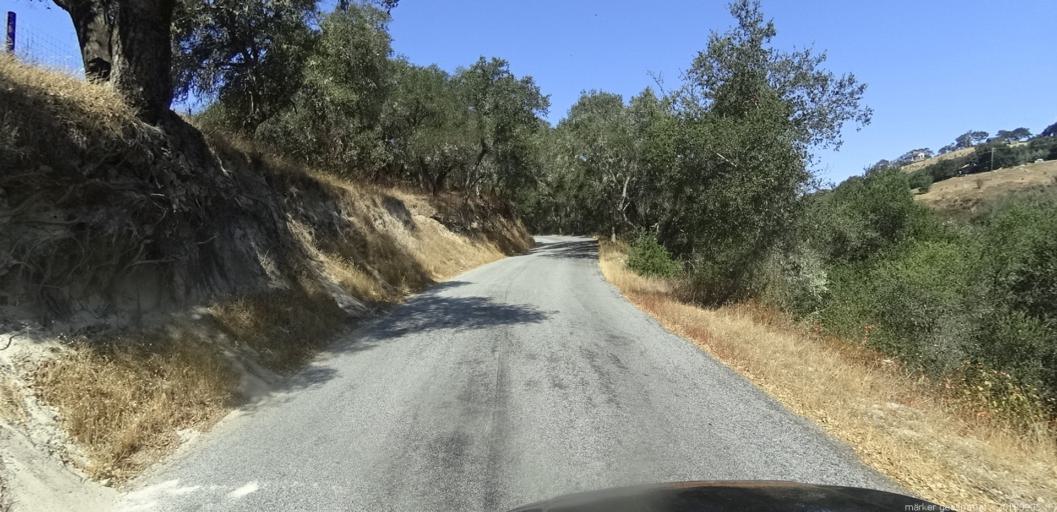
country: US
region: California
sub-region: Monterey County
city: Carmel Valley Village
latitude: 36.4230
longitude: -121.6816
